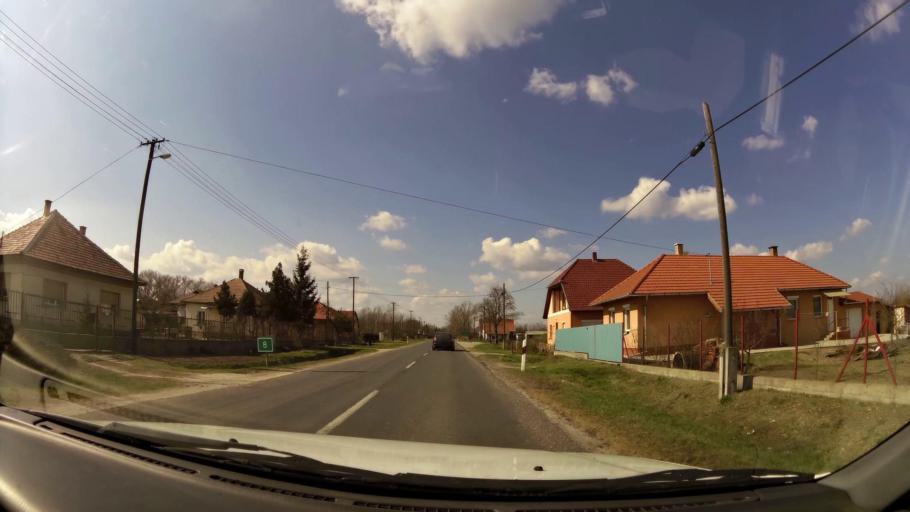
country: HU
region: Pest
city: Farmos
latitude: 47.3633
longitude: 19.8090
